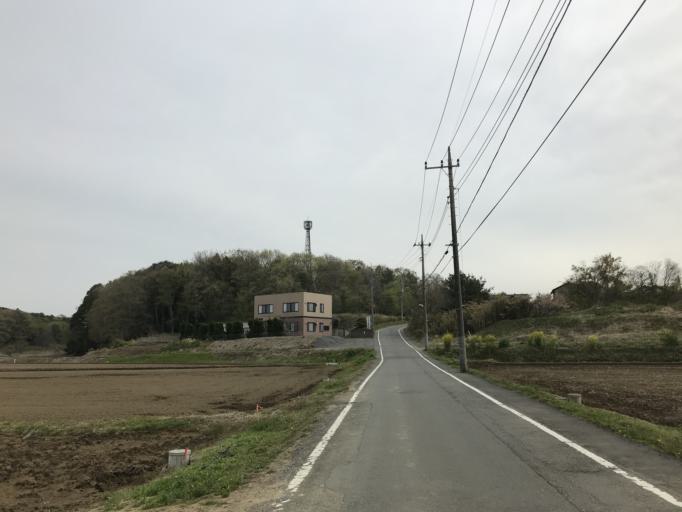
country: JP
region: Ibaraki
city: Moriya
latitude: 35.9528
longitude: 140.0086
